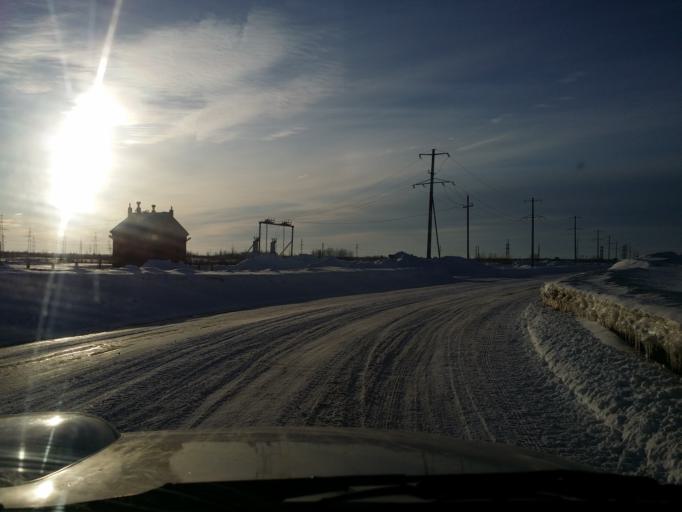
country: RU
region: Khanty-Mansiyskiy Avtonomnyy Okrug
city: Izluchinsk
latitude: 60.9725
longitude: 76.9442
